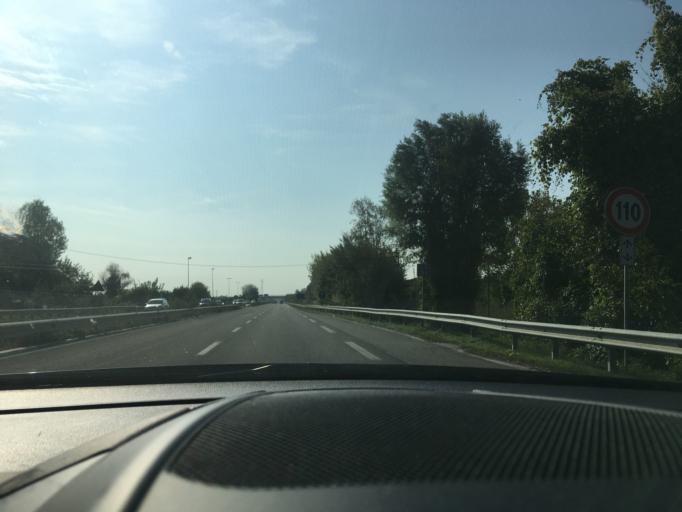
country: IT
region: Emilia-Romagna
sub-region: Provincia di Rimini
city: Bellaria-Igea Marina
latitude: 44.1419
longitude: 12.4575
